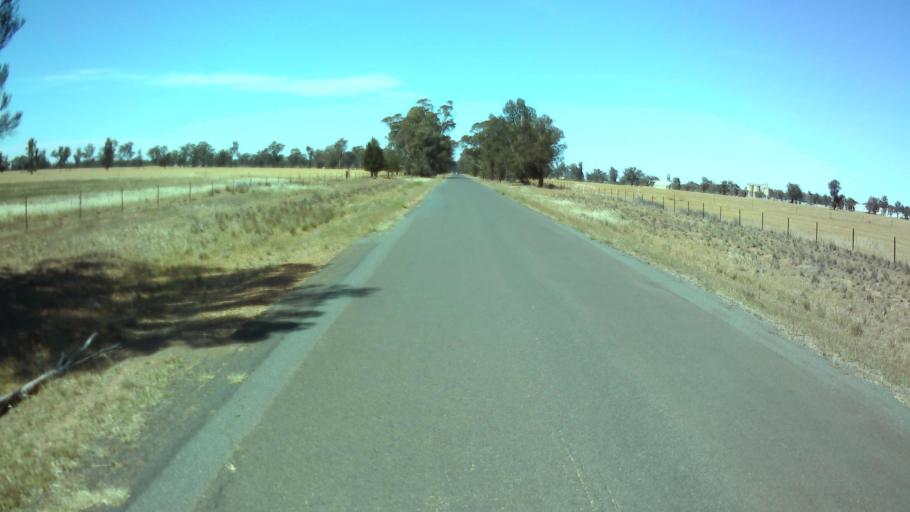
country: AU
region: New South Wales
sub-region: Weddin
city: Grenfell
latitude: -34.1072
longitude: 147.8864
